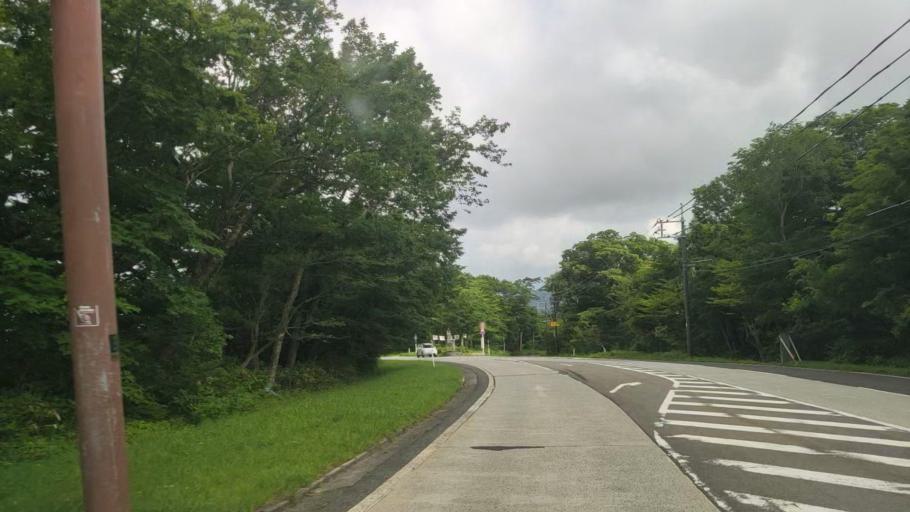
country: JP
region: Tottori
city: Yonago
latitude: 35.3947
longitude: 133.5273
